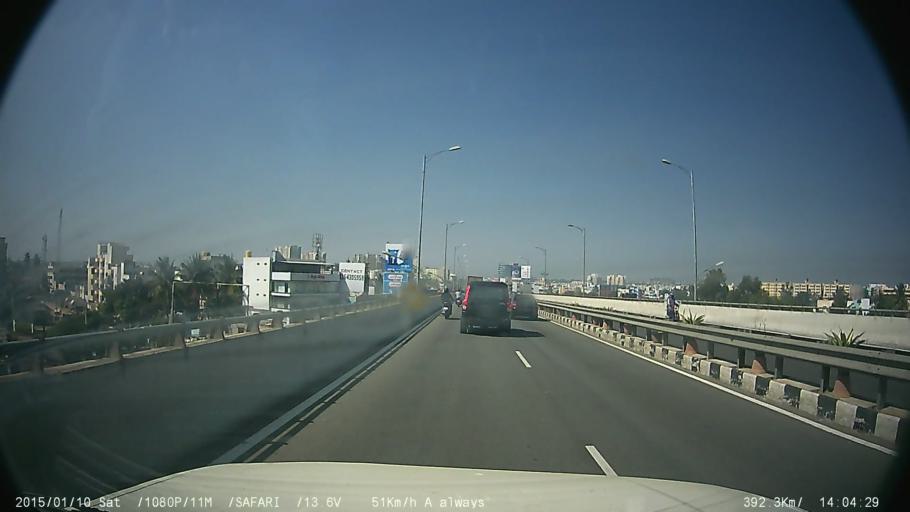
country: IN
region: Karnataka
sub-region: Bangalore Urban
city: Bangalore
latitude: 12.8924
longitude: 77.6379
